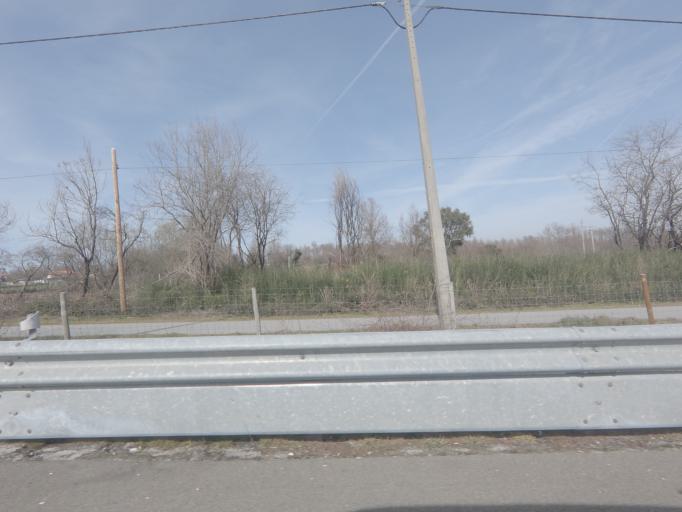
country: PT
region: Viseu
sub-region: Oliveira de Frades
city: Oliveira de Frades
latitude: 40.6873
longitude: -8.2330
